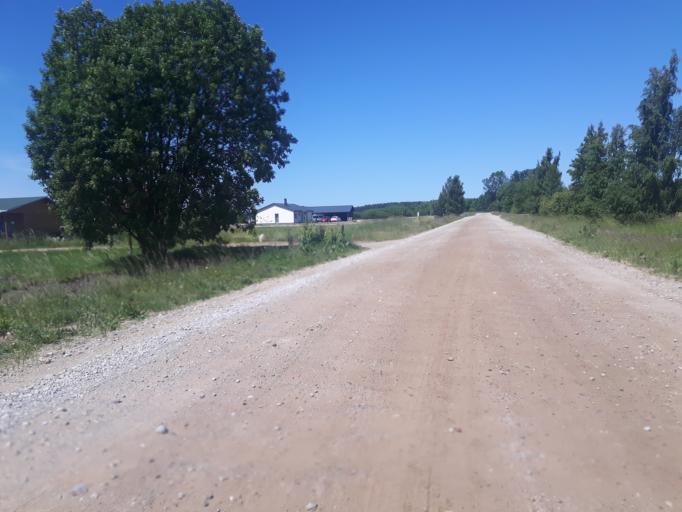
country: LV
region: Grobina
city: Grobina
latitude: 56.5295
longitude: 21.1304
